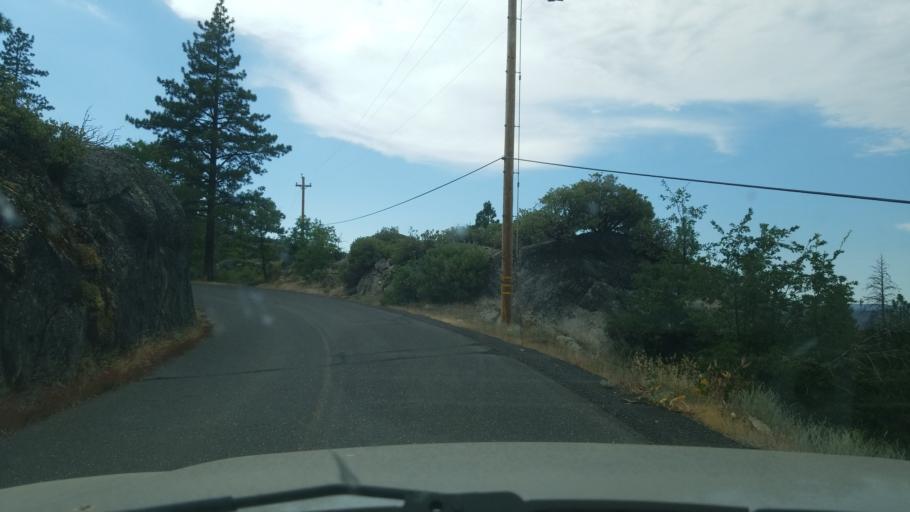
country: US
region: California
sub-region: Mariposa County
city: Yosemite Valley
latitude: 37.9033
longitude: -119.8172
